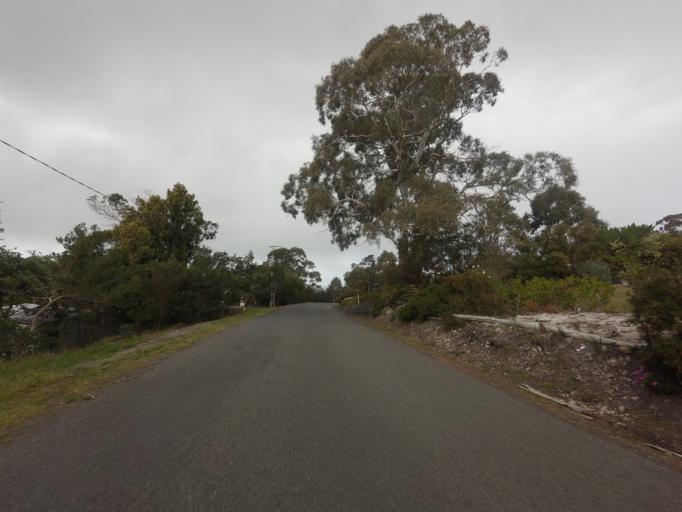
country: AU
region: Tasmania
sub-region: Sorell
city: Sorell
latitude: -42.5317
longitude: 147.9119
